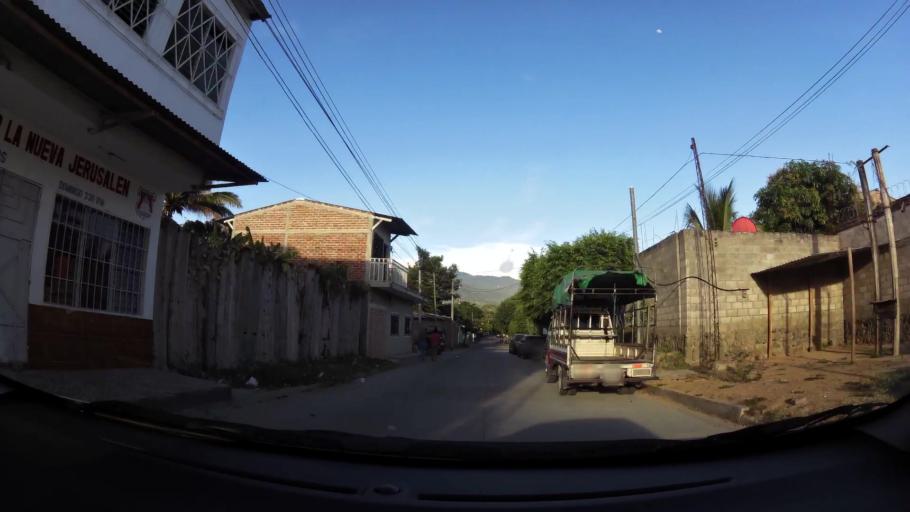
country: SV
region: Santa Ana
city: Metapan
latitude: 14.3315
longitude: -89.4535
